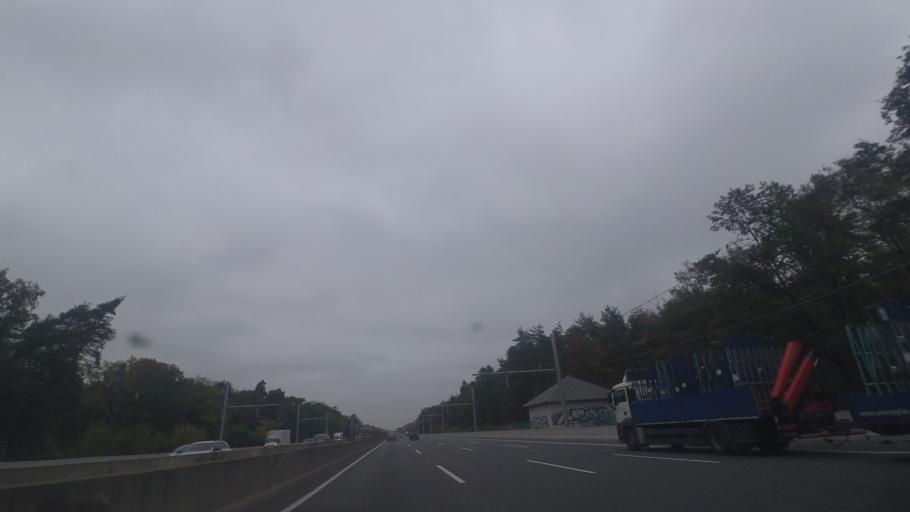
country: DE
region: Hesse
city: Morfelden-Walldorf
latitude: 49.9626
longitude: 8.6065
